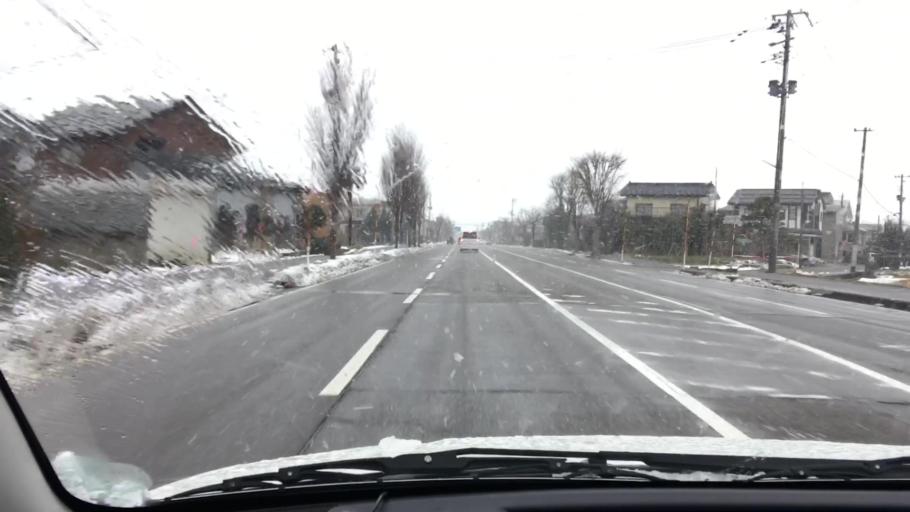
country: JP
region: Niigata
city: Joetsu
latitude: 37.1182
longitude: 138.2328
